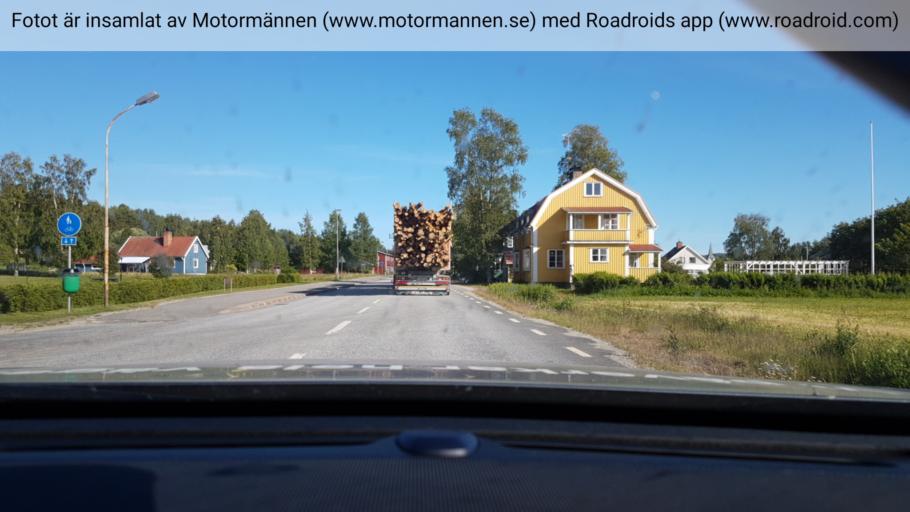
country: SE
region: Vaesterbotten
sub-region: Bjurholms Kommun
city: Bjurholm
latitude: 64.2475
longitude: 19.3169
